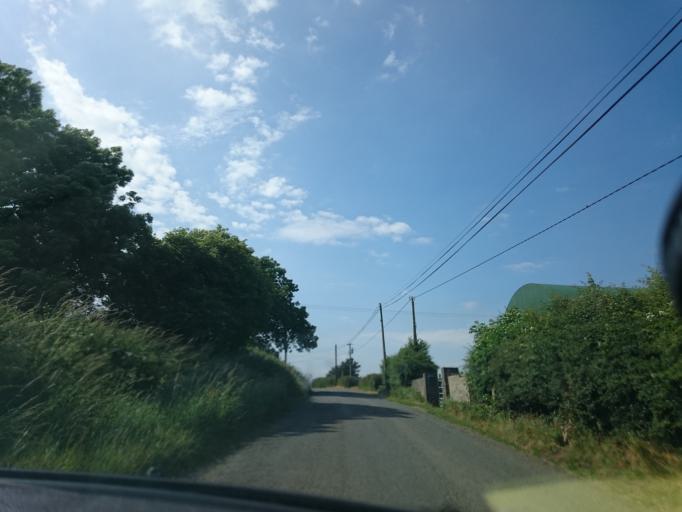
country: IE
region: Leinster
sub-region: Kilkenny
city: Thomastown
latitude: 52.5278
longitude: -7.2071
